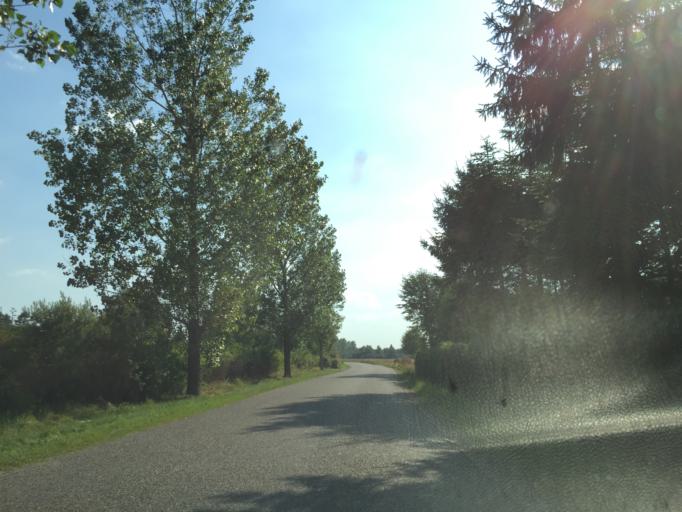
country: DK
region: Central Jutland
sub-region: Viborg Kommune
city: Bjerringbro
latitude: 56.2857
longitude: 9.6784
